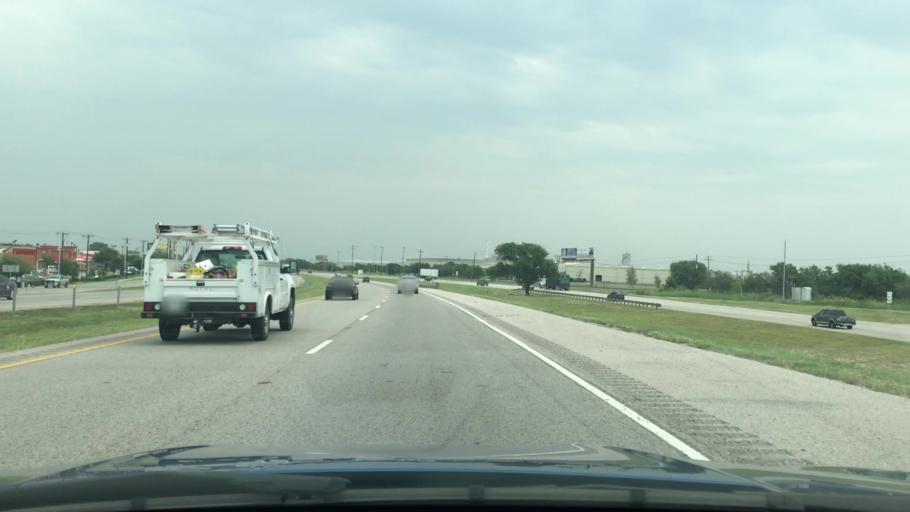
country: US
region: Texas
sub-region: Kaufman County
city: Forney
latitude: 32.7421
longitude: -96.4471
